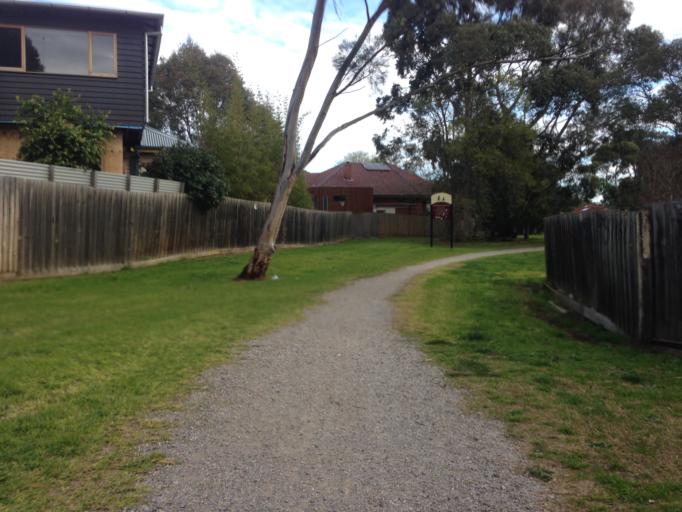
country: AU
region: Victoria
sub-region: Banyule
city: Bellfield
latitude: -37.7573
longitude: 145.0437
